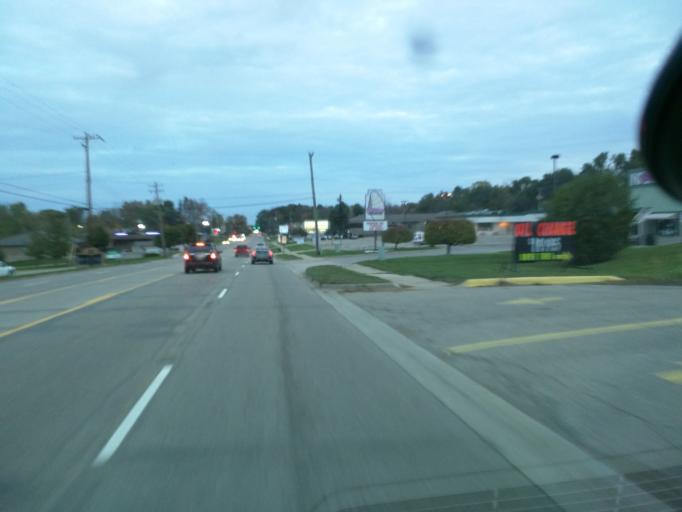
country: US
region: Michigan
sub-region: Ingham County
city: Edgemont Park
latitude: 42.7301
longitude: -84.6029
